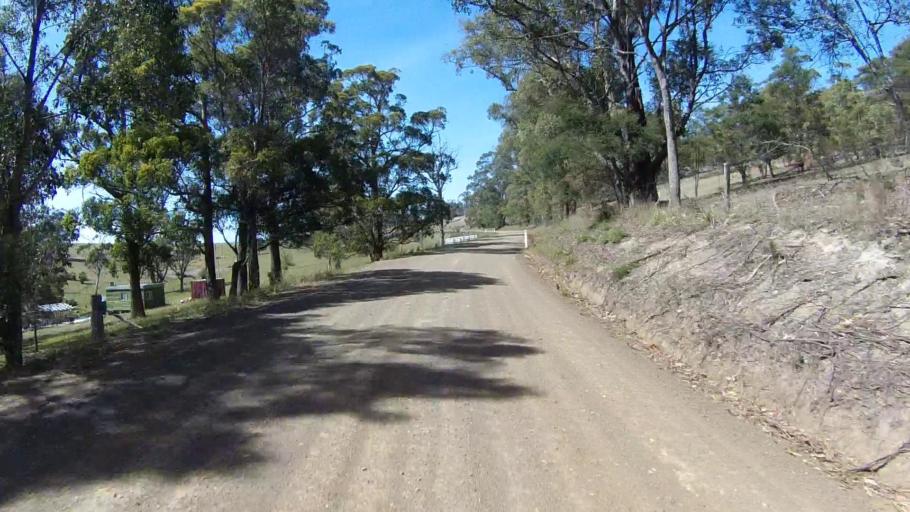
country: AU
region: Tasmania
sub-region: Sorell
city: Sorell
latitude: -42.7374
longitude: 147.5981
